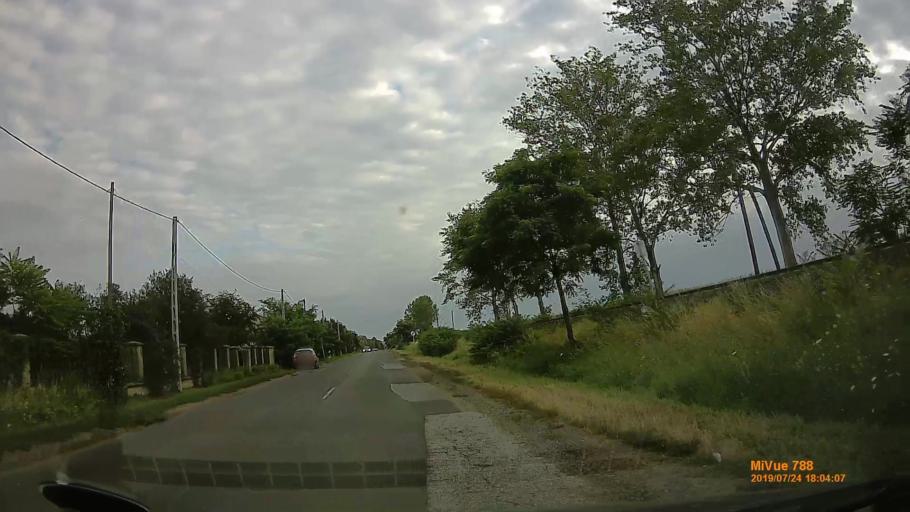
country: HU
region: Borsod-Abauj-Zemplen
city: Abaujszanto
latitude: 48.3054
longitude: 21.1980
